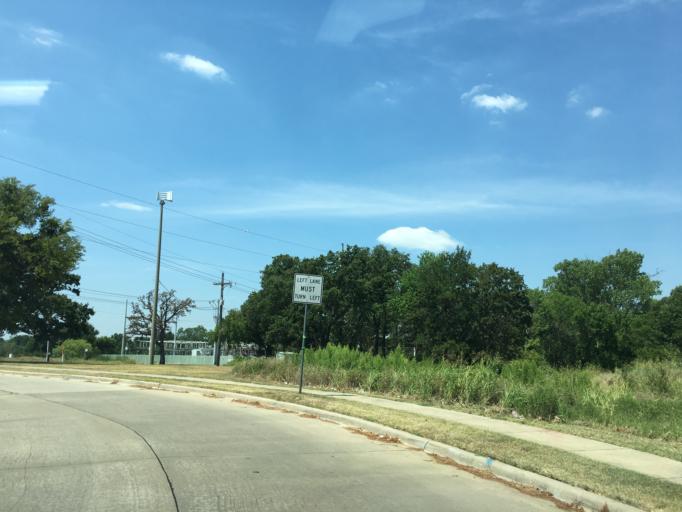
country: US
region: Texas
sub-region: Denton County
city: Lewisville
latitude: 33.0279
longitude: -96.9991
